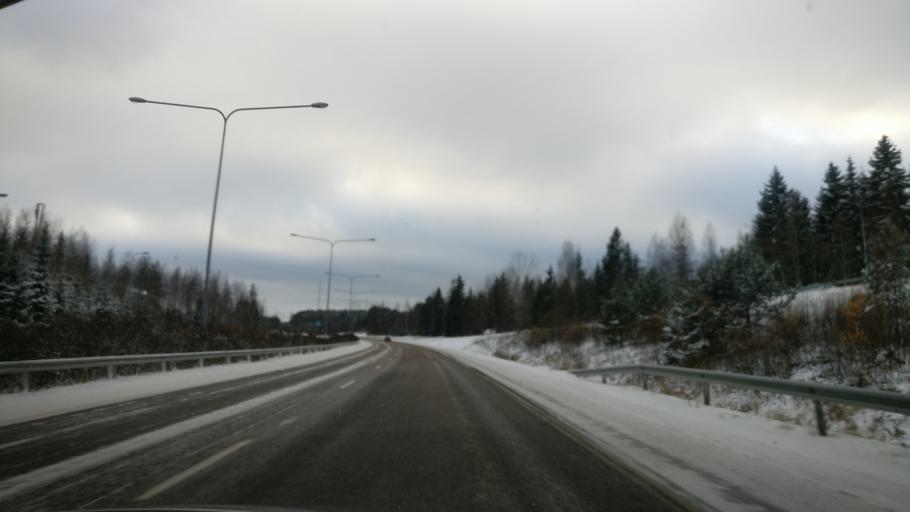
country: FI
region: Paijanne Tavastia
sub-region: Lahti
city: Lahti
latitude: 60.9858
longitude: 25.7358
